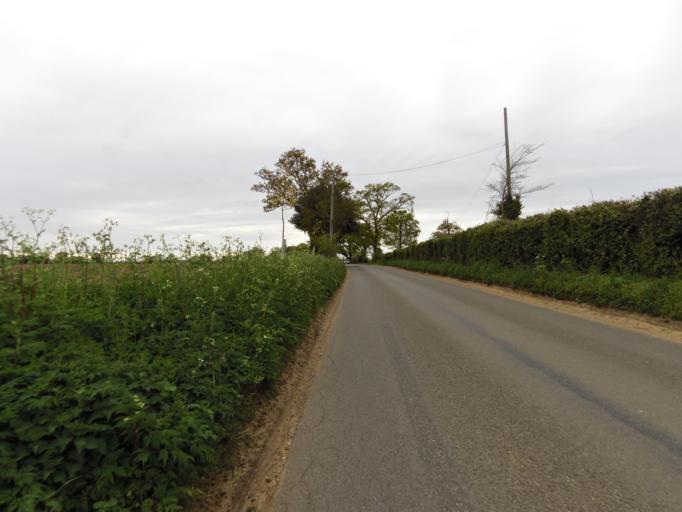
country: GB
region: England
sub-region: Suffolk
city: Kesgrave
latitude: 52.0157
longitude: 1.2238
